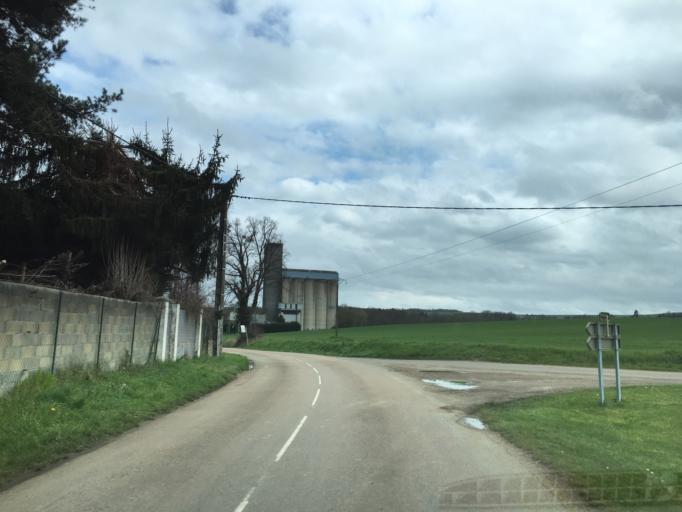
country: FR
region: Bourgogne
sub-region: Departement de l'Yonne
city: Pourrain
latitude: 47.7922
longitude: 3.3895
